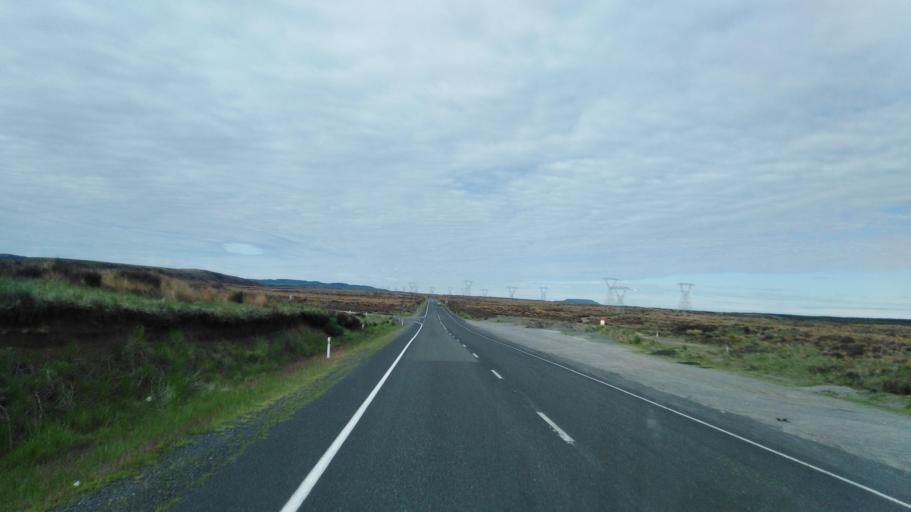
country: NZ
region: Manawatu-Wanganui
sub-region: Ruapehu District
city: Waiouru
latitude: -39.3911
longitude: 175.7054
